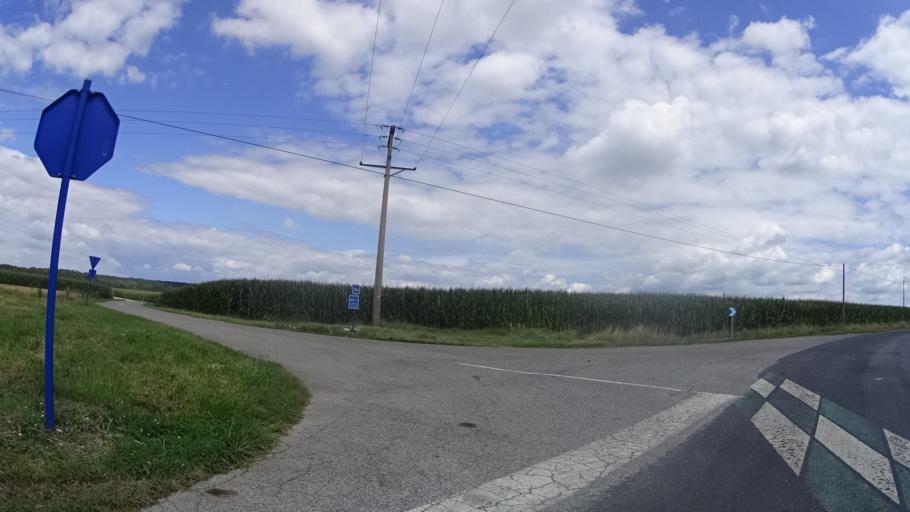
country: FR
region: Champagne-Ardenne
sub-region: Departement de la Haute-Marne
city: Montier-en-Der
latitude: 48.5119
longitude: 4.7745
